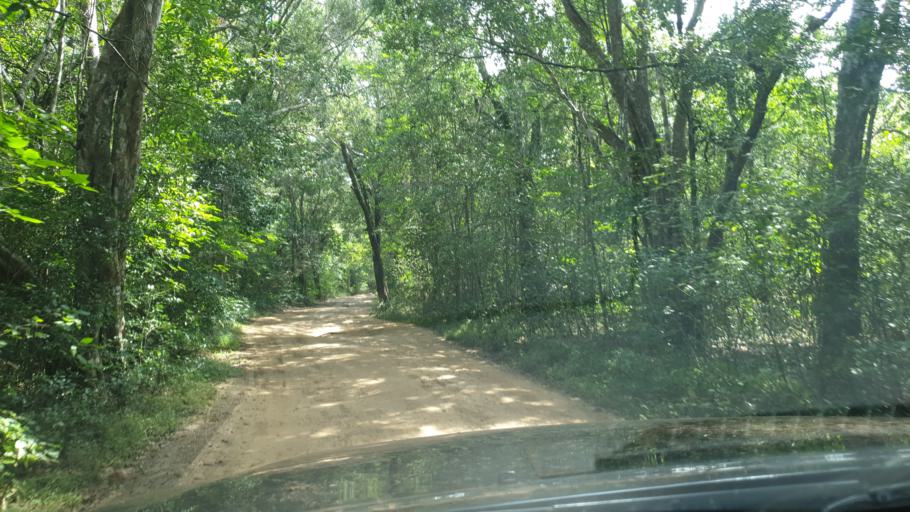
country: LK
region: North Central
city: Anuradhapura
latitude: 8.4205
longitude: 80.0236
